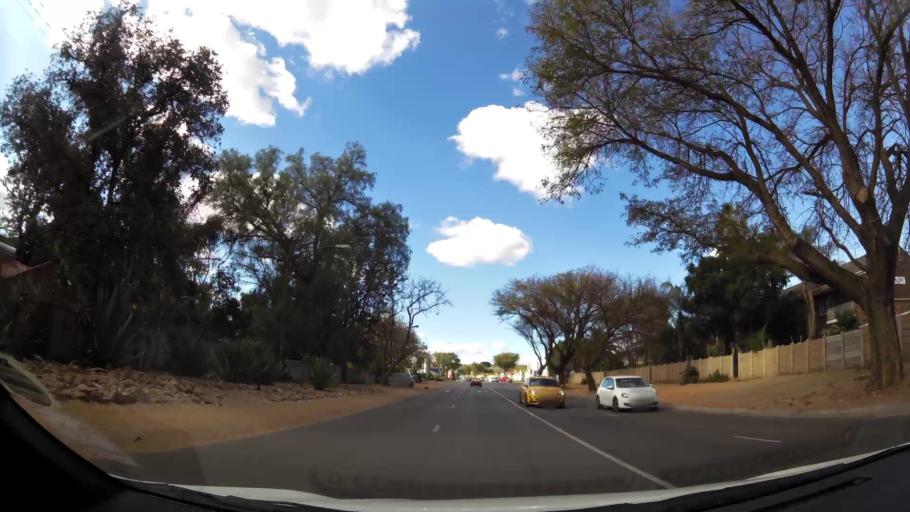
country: ZA
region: Limpopo
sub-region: Capricorn District Municipality
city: Polokwane
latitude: -23.8931
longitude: 29.4709
